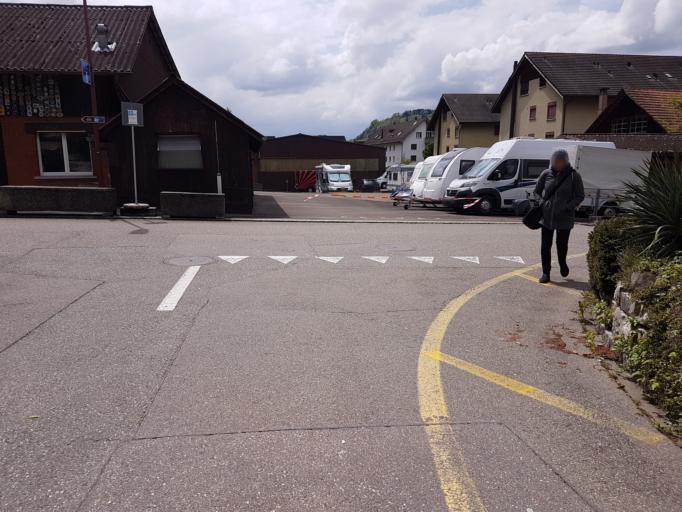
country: CH
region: Aargau
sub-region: Bezirk Brugg
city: Lauffohr (Brugg)
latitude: 47.5183
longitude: 8.2425
